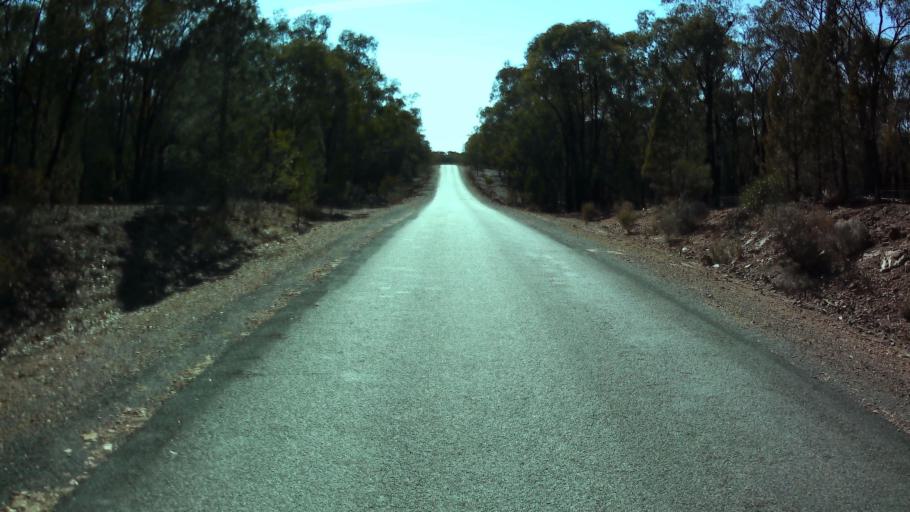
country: AU
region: New South Wales
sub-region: Weddin
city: Grenfell
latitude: -33.7848
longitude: 147.9855
